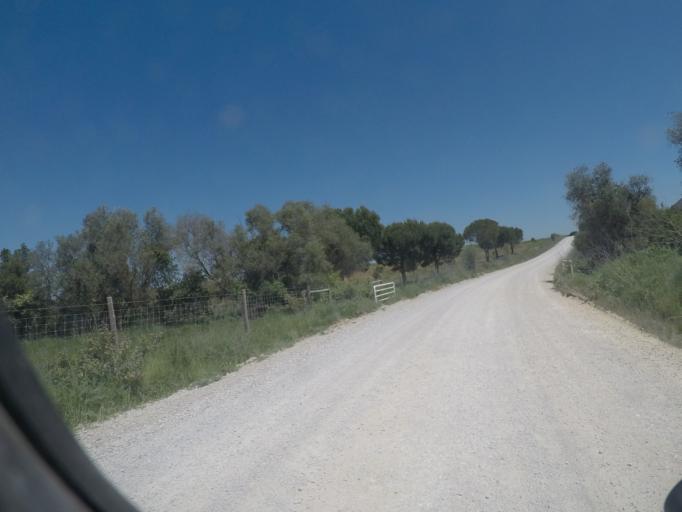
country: PT
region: Setubal
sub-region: Sesimbra
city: Sesimbra
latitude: 38.4694
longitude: -9.0445
